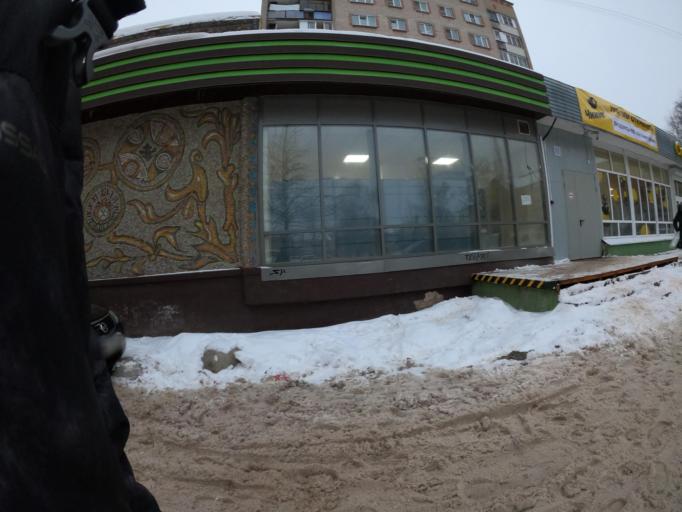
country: RU
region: Moskovskaya
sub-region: Podol'skiy Rayon
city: Podol'sk
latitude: 55.4148
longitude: 37.5433
